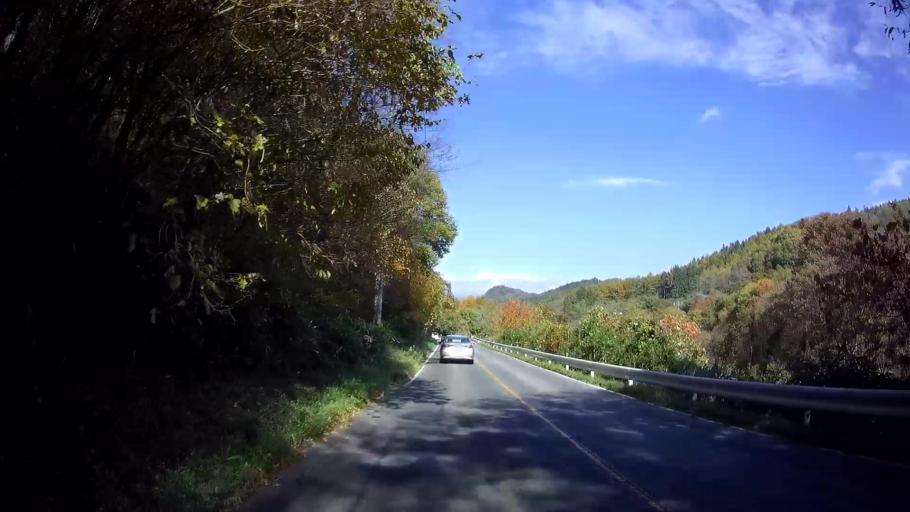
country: JP
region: Gunma
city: Nakanojomachi
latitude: 36.4982
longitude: 138.7768
